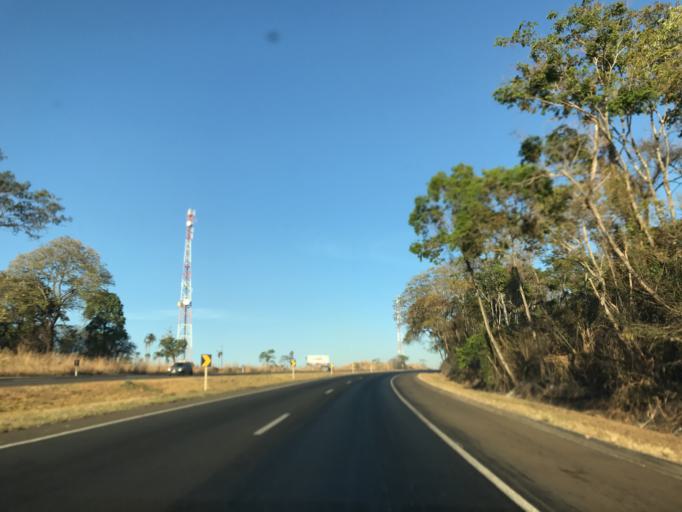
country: BR
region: Goias
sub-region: Goiania
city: Goiania
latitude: -16.5806
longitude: -49.1675
